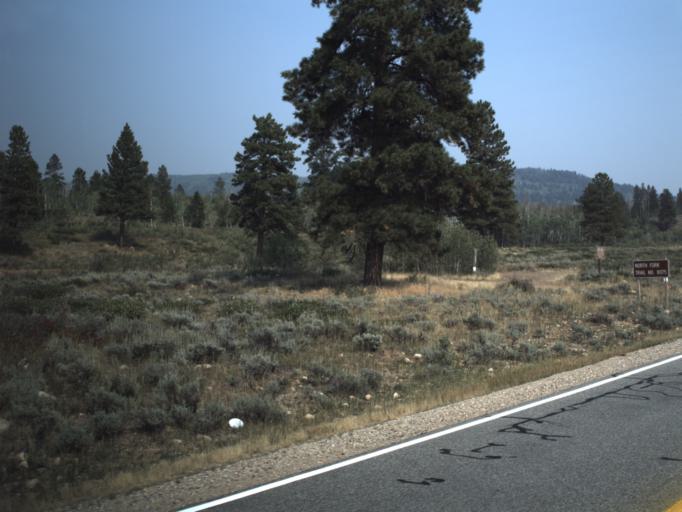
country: US
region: Utah
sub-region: Summit County
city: Francis
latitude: 40.5962
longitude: -111.0944
